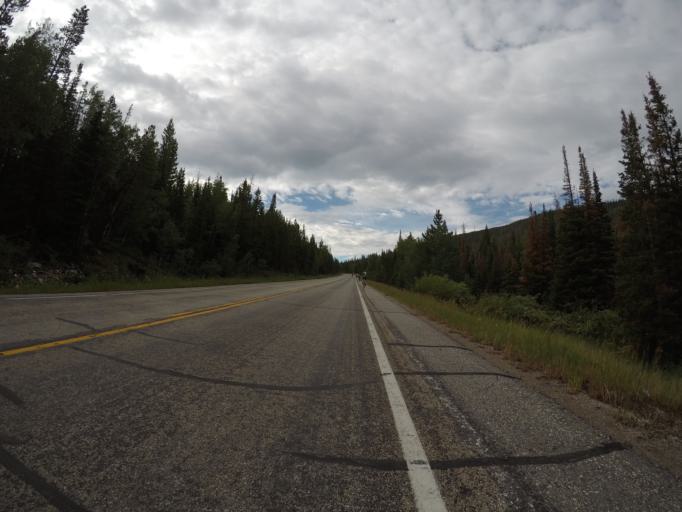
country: US
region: Wyoming
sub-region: Carbon County
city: Saratoga
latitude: 41.3395
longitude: -106.5246
